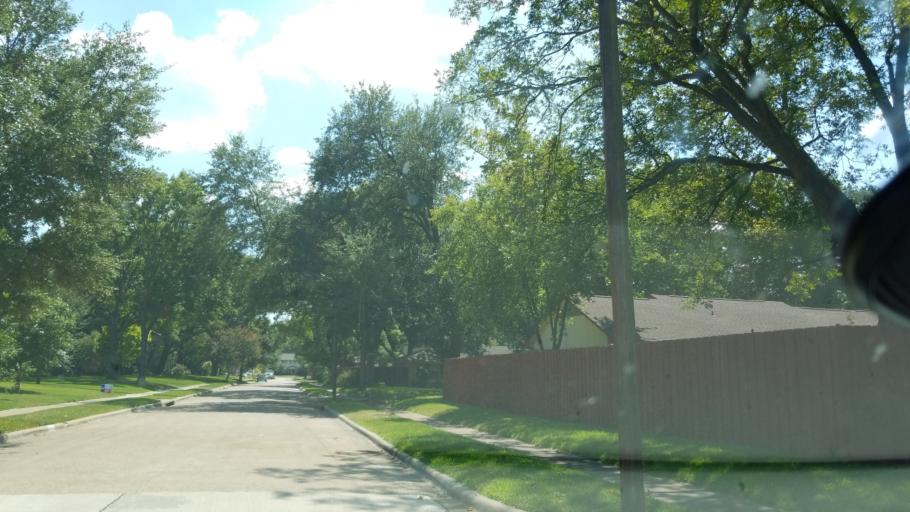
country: US
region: Texas
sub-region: Dallas County
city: Richardson
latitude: 32.8817
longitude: -96.7130
